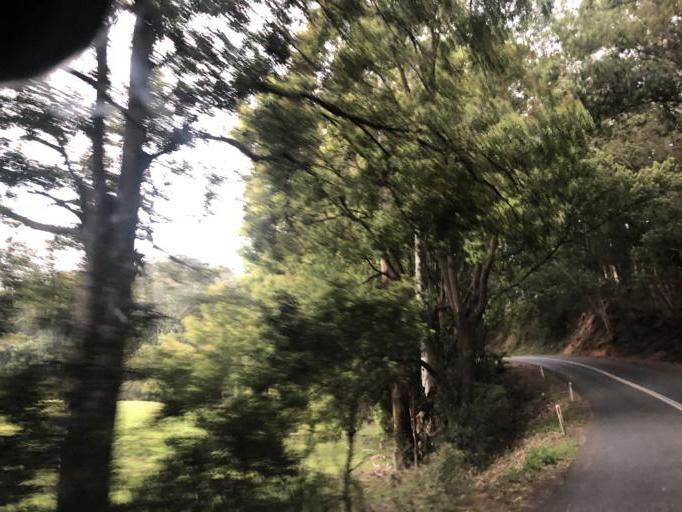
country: AU
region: New South Wales
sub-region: Coffs Harbour
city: Boambee
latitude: -30.2636
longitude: 153.0175
